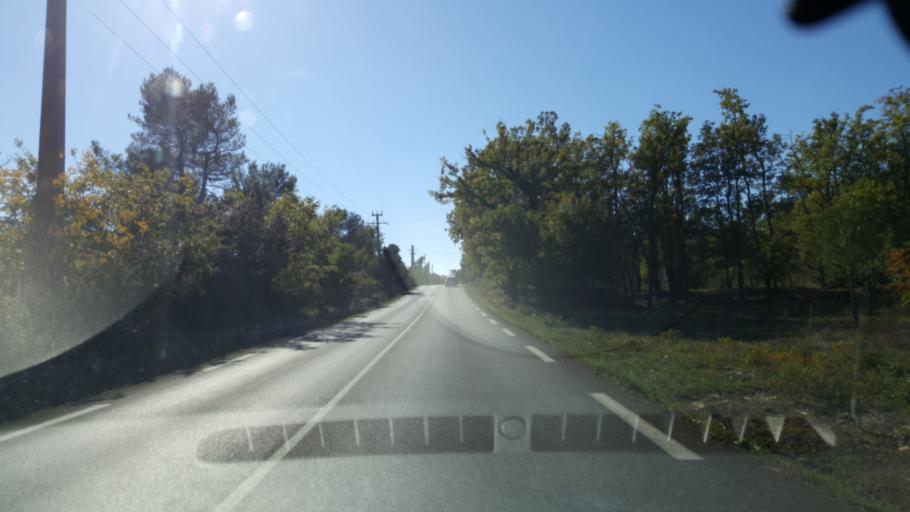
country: FR
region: Provence-Alpes-Cote d'Azur
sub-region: Departement du Var
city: Saint-Maximin-la-Sainte-Baume
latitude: 43.4279
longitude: 5.8468
